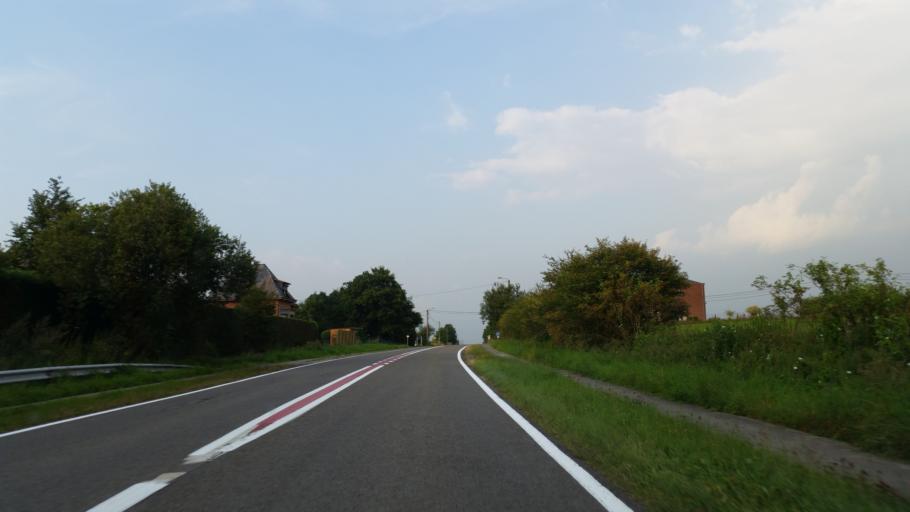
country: BE
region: Wallonia
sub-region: Province du Luxembourg
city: Durbuy
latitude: 50.3236
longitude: 5.4203
